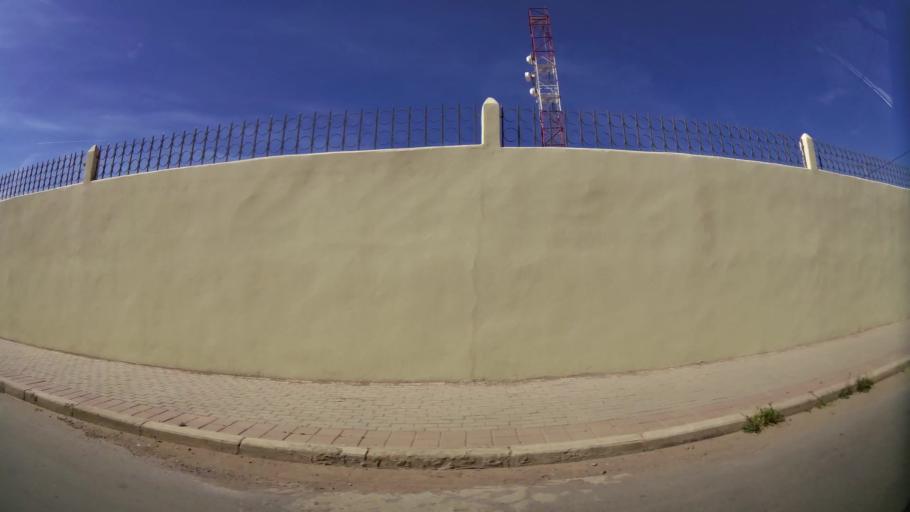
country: MA
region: Oriental
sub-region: Oujda-Angad
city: Oujda
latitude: 34.6605
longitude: -1.9144
